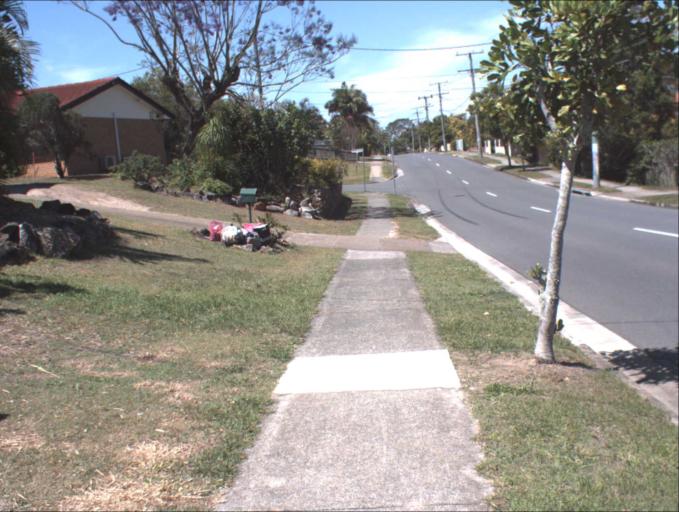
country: AU
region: Queensland
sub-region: Logan
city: Springwood
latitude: -27.6066
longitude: 153.1267
